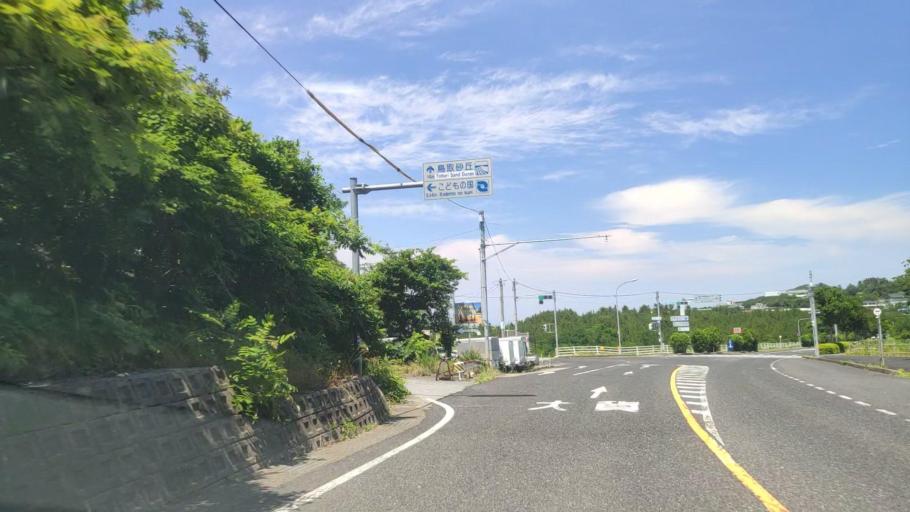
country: JP
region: Tottori
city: Tottori
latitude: 35.5331
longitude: 134.2303
